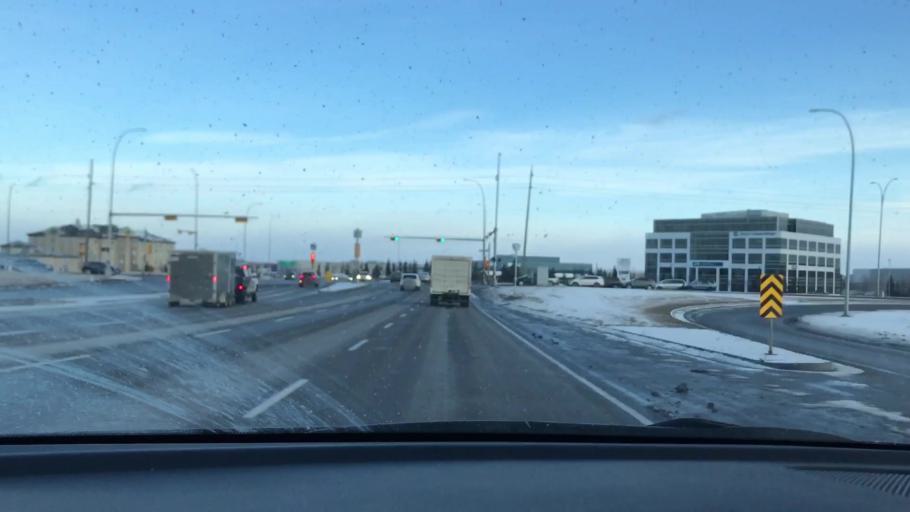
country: CA
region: Alberta
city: Calgary
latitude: 51.0927
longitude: -114.0039
